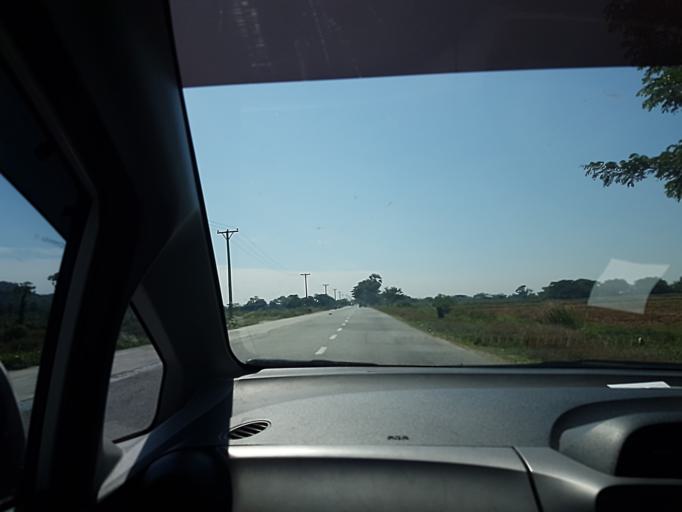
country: MM
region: Mon
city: Thaton
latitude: 16.8717
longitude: 97.3598
